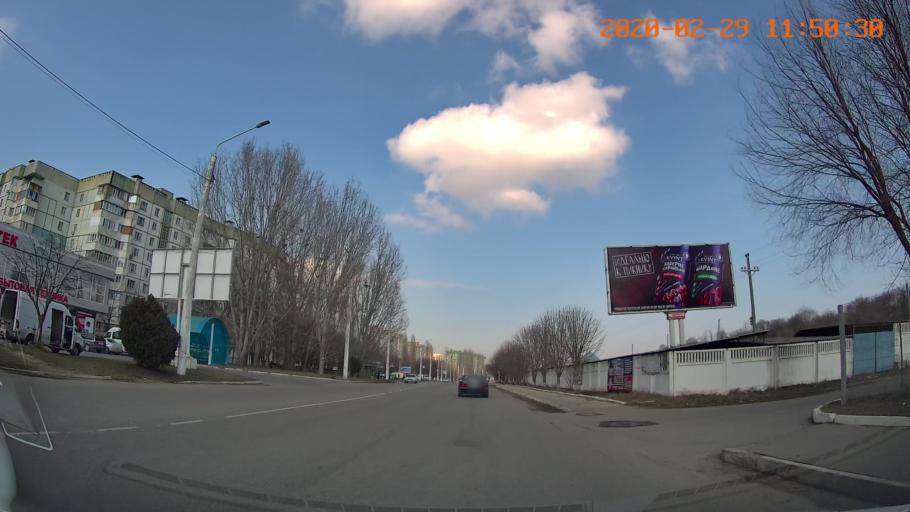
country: MD
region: Telenesti
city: Ribnita
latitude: 47.7584
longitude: 28.9906
